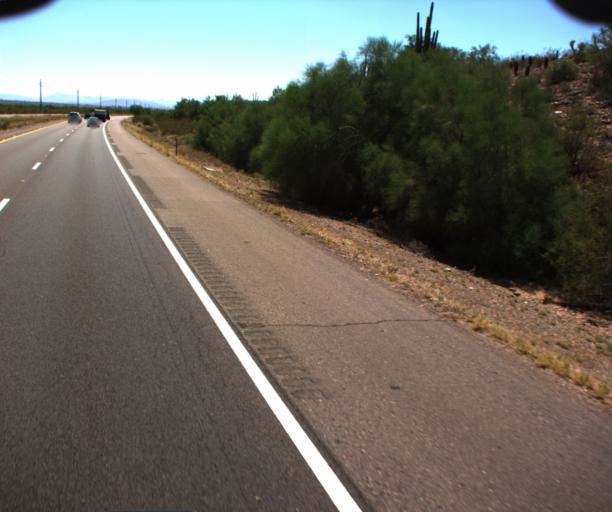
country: US
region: Arizona
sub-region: Maricopa County
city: Fountain Hills
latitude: 33.5206
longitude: -111.7428
